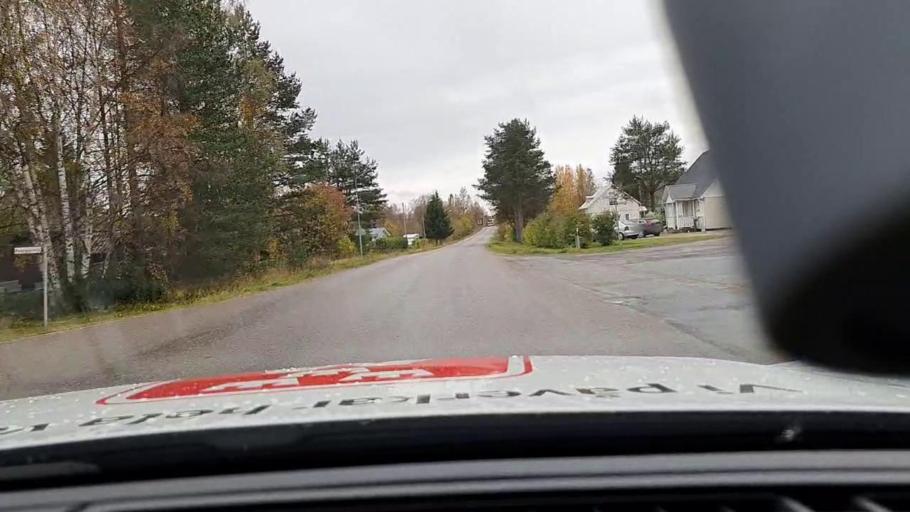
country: SE
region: Norrbotten
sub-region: Haparanda Kommun
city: Haparanda
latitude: 65.8032
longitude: 23.9187
